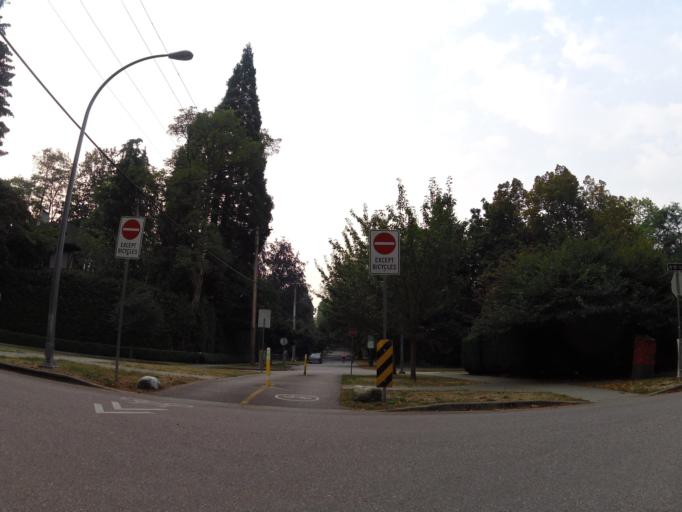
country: CA
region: British Columbia
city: Vancouver
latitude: 49.2546
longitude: -123.1485
